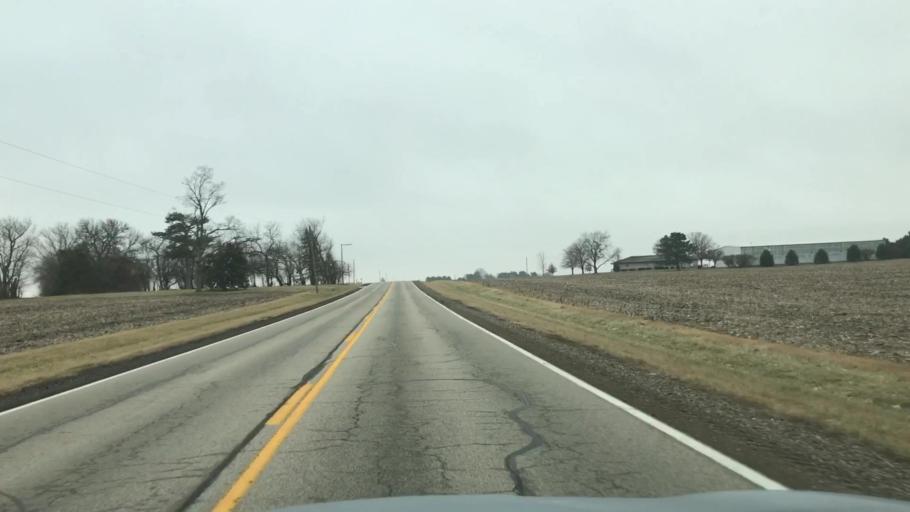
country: US
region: Illinois
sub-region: McLean County
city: Hudson
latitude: 40.5939
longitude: -88.9448
